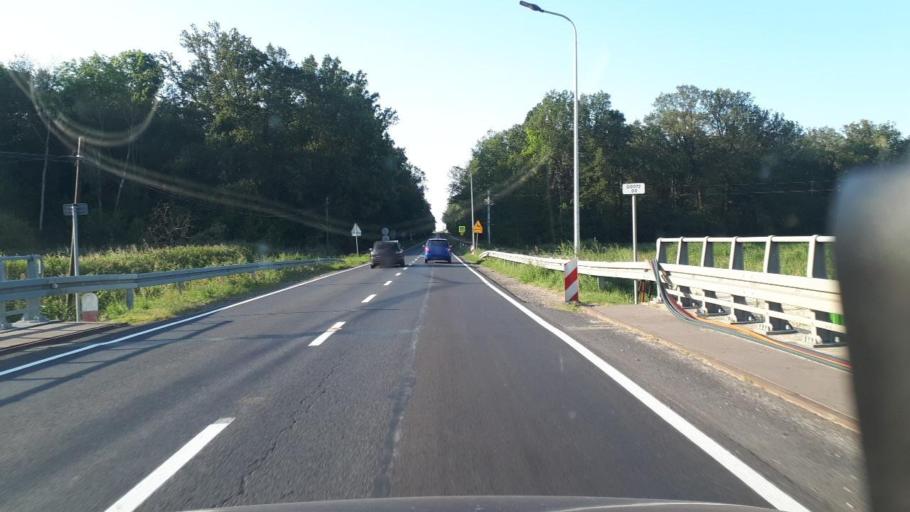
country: PL
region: Silesian Voivodeship
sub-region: Powiat lubliniecki
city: Ciasna
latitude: 50.7561
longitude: 18.6081
